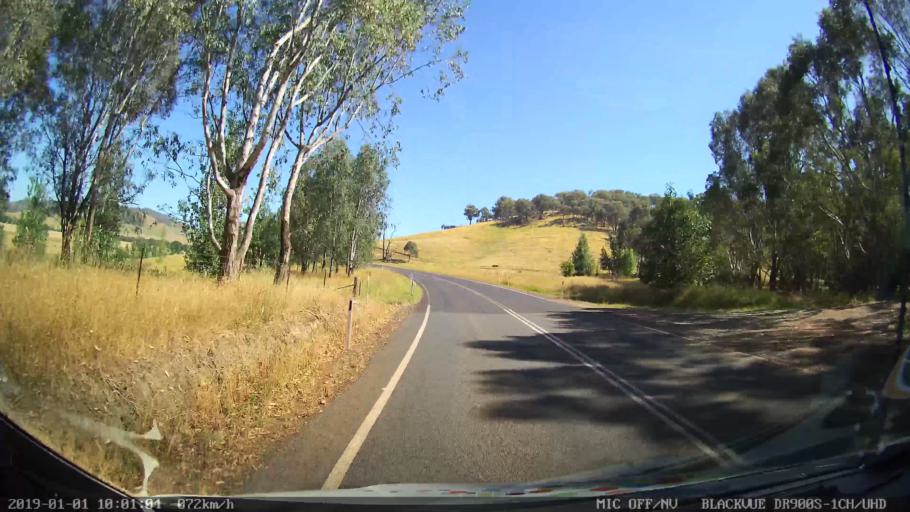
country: AU
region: New South Wales
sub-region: Snowy River
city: Jindabyne
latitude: -36.1953
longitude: 148.1031
